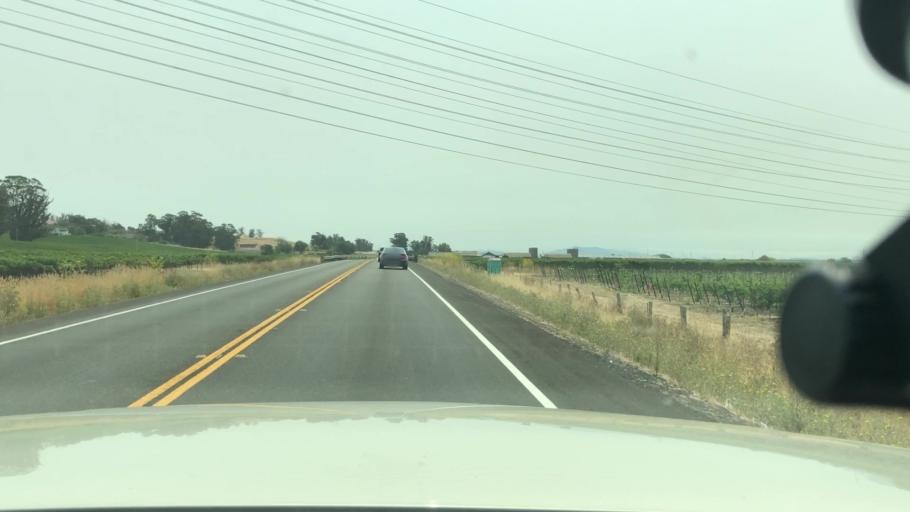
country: US
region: California
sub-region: Marin County
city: Black Point-Green Point
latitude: 38.1628
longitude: -122.5063
